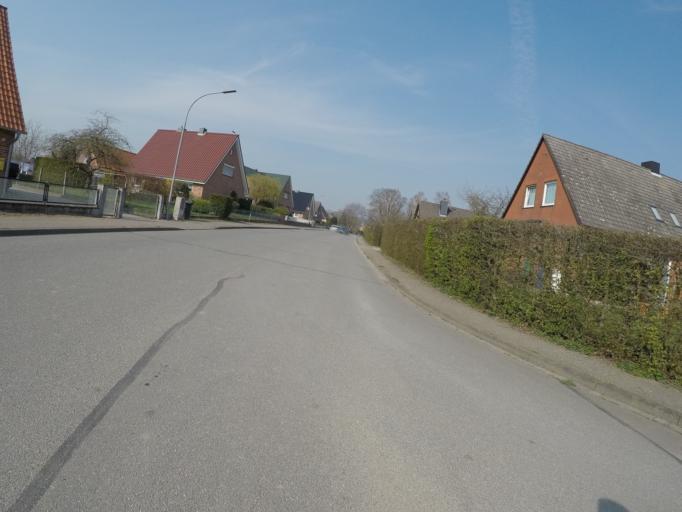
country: DE
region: Schleswig-Holstein
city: Gross Niendorf
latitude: 53.8426
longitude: 10.2401
